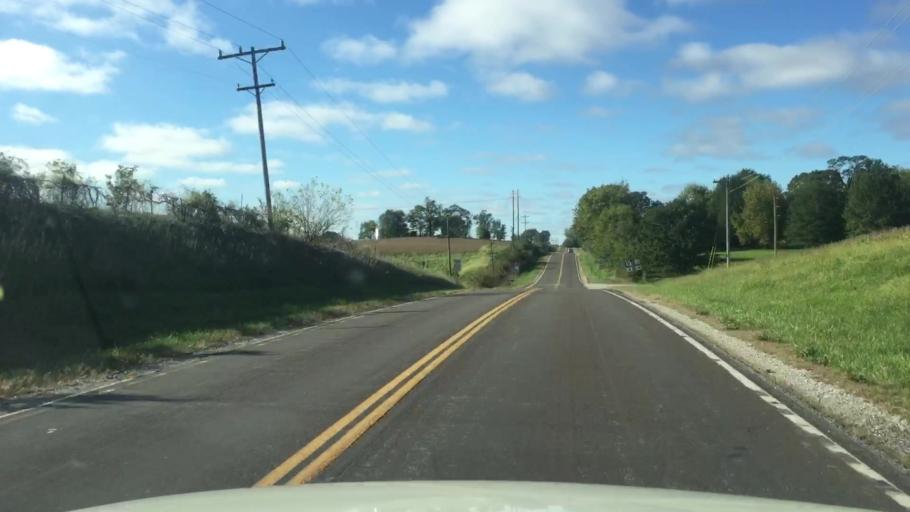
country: US
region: Missouri
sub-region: Howard County
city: Fayette
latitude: 39.1052
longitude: -92.7335
